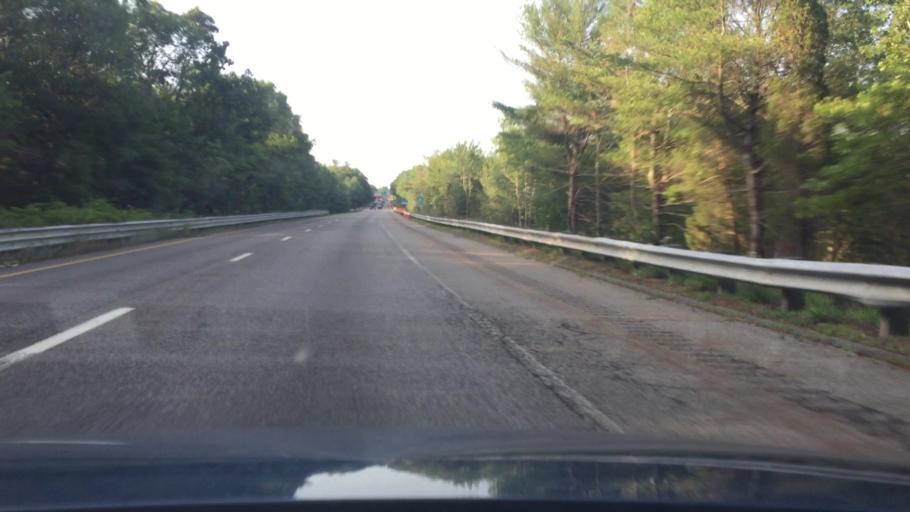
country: US
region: Massachusetts
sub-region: Plymouth County
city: Marshfield
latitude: 42.0631
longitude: -70.7276
